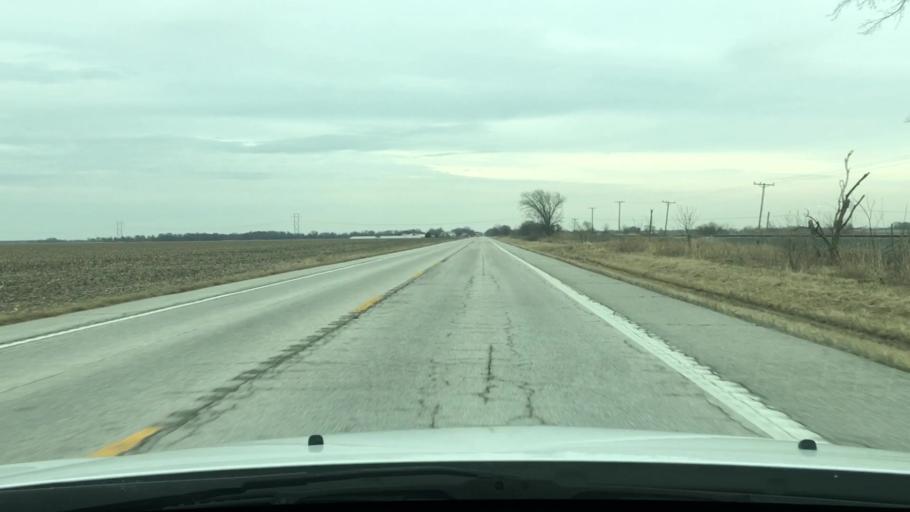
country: US
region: Missouri
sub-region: Audrain County
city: Vandalia
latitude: 39.2868
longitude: -91.5416
